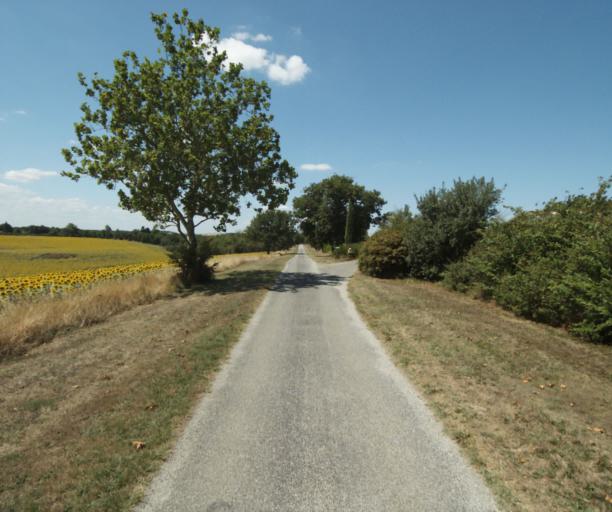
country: FR
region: Midi-Pyrenees
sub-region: Departement de la Haute-Garonne
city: Saint-Felix-Lauragais
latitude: 43.4759
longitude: 1.8638
